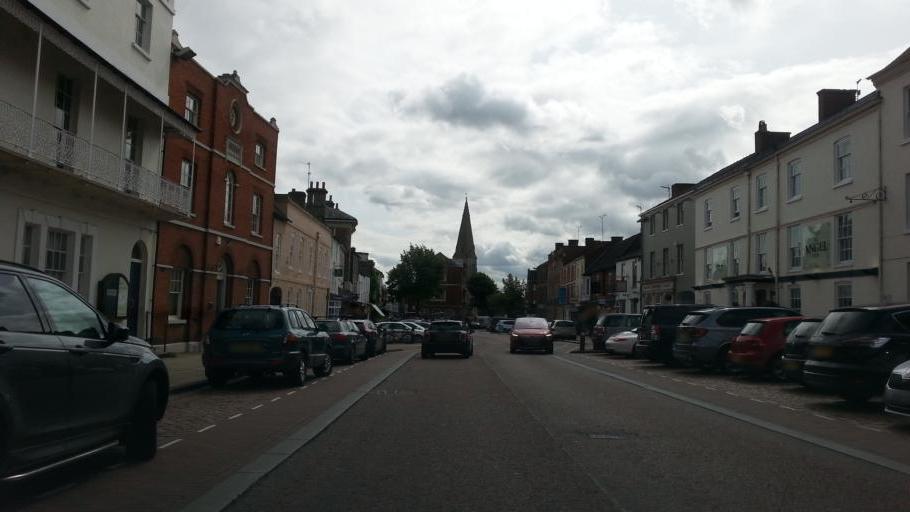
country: GB
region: England
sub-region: Leicestershire
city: Market Harborough
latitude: 52.4805
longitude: -0.9237
